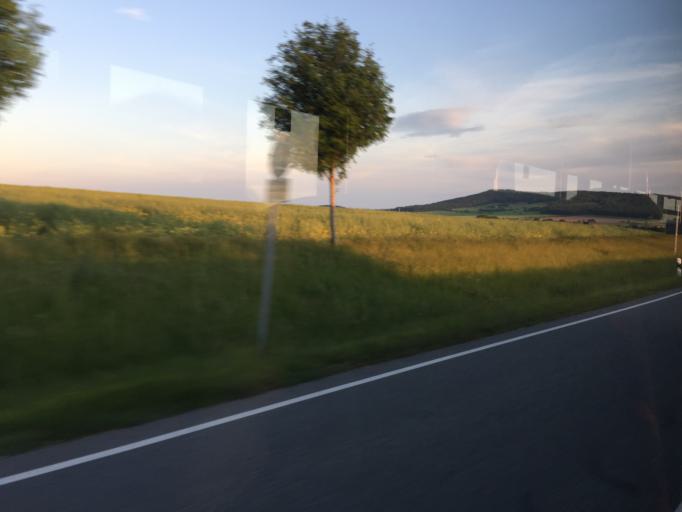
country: DE
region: Saxony
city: Reichenbach
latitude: 51.1459
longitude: 14.7756
